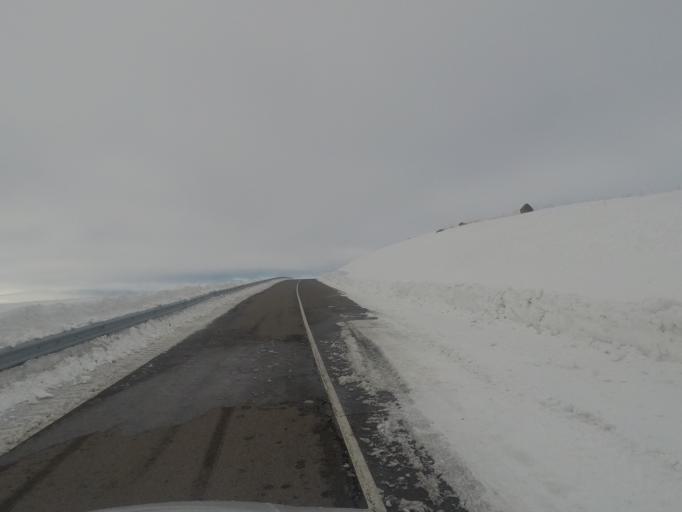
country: GE
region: Kvemo Kartli
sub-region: Tsalka
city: Tsalka
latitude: 41.4355
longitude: 43.8440
